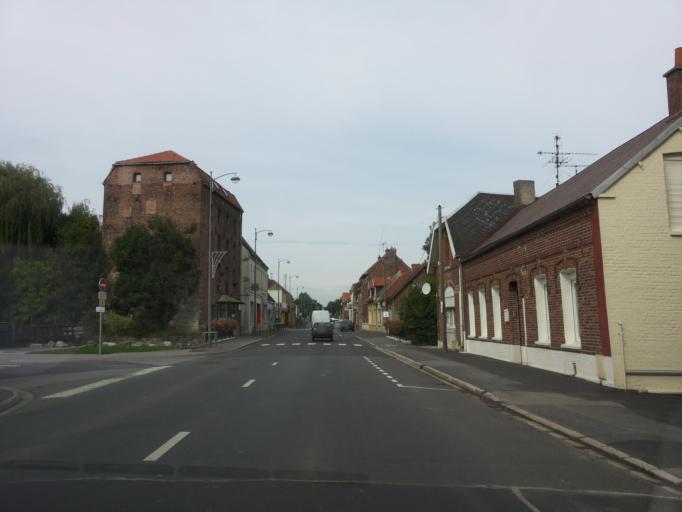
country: FR
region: Nord-Pas-de-Calais
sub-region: Departement du Pas-de-Calais
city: Marquion
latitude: 50.2119
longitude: 3.0834
